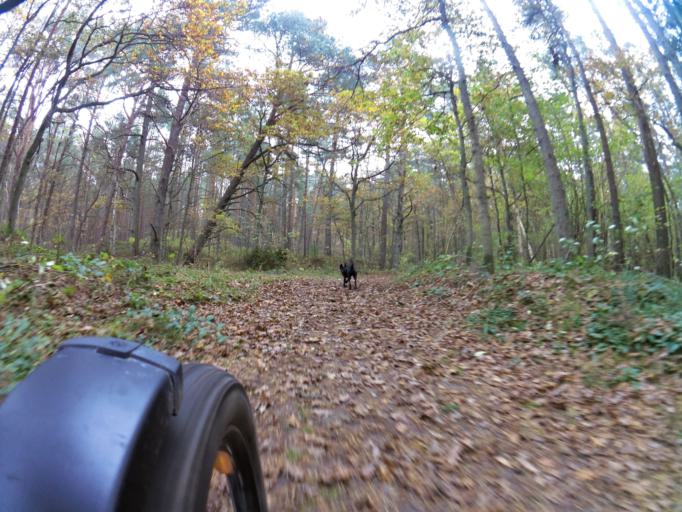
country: PL
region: Pomeranian Voivodeship
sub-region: Powiat pucki
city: Krokowa
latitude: 54.8298
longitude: 18.1177
